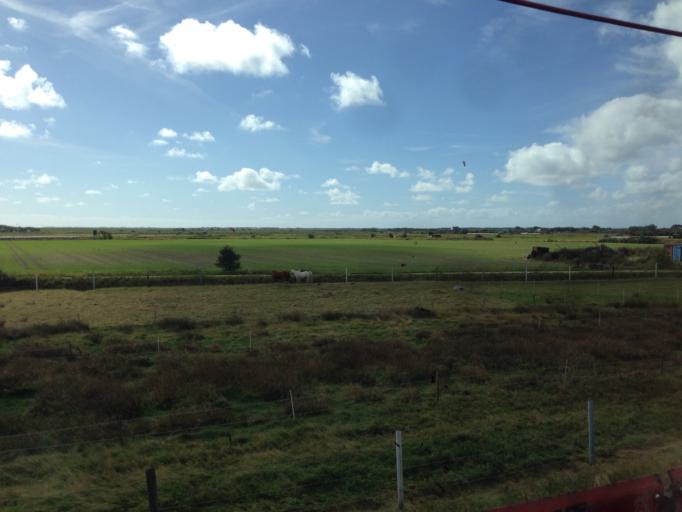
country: DE
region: Schleswig-Holstein
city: Tinnum
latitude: 54.8964
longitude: 8.3455
